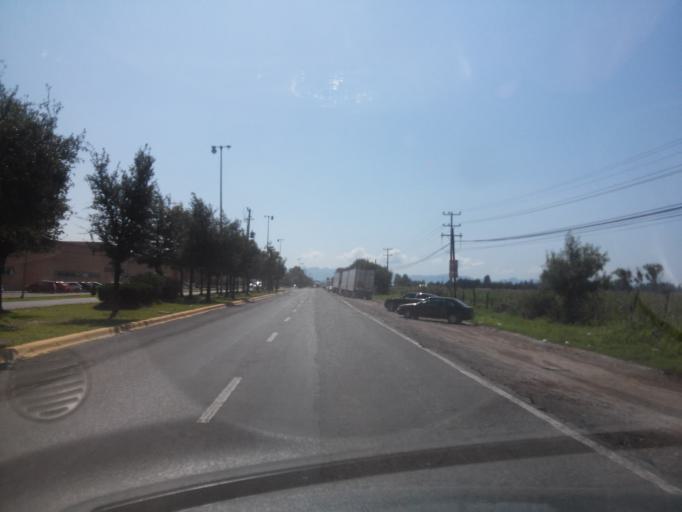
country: MX
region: Durango
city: Victoria de Durango
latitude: 23.9932
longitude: -104.6293
